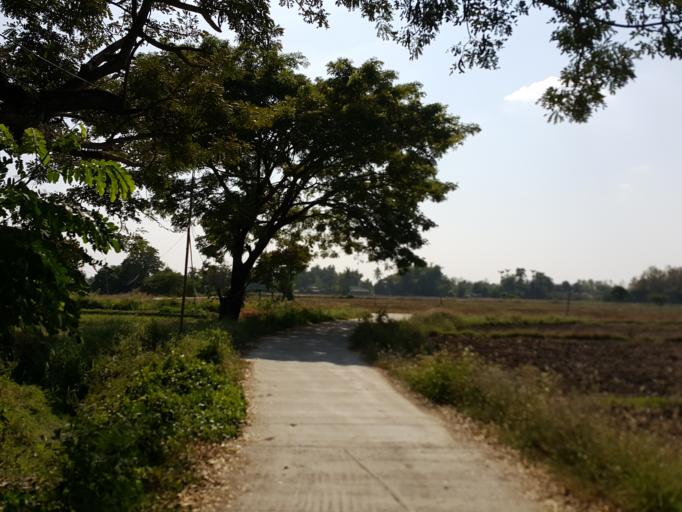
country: TH
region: Chiang Mai
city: San Kamphaeng
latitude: 18.8127
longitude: 99.1593
